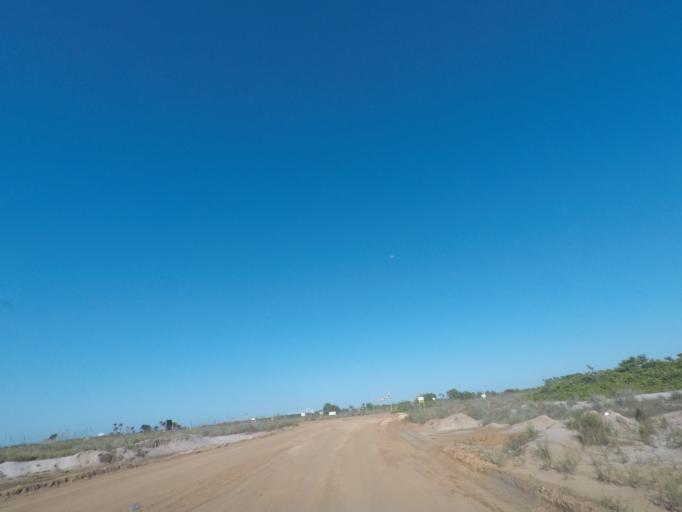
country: BR
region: Bahia
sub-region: Camamu
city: Camamu
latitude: -13.9421
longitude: -38.9460
